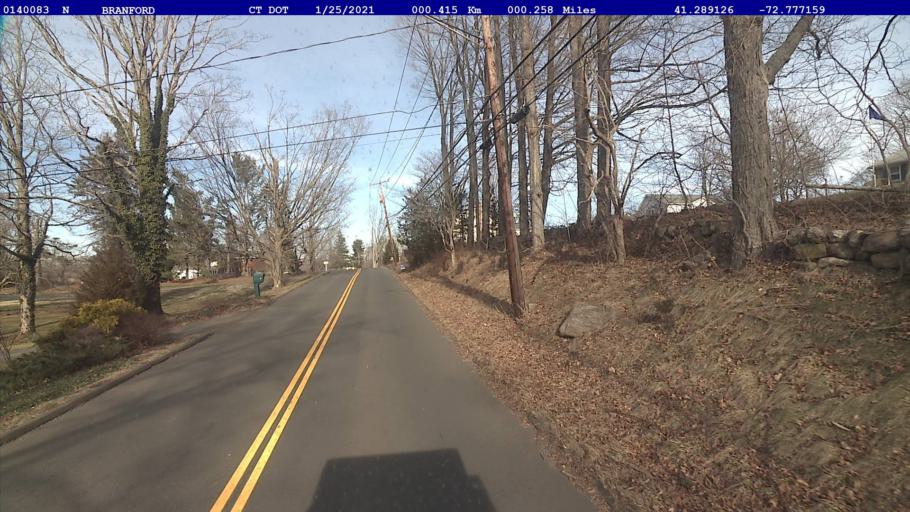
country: US
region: Connecticut
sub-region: New Haven County
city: Branford
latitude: 41.2891
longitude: -72.7772
